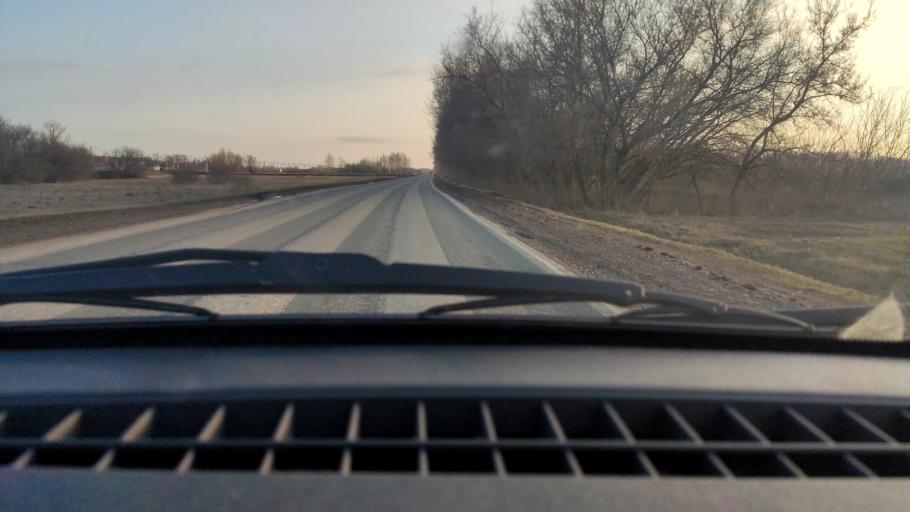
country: RU
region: Bashkortostan
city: Chishmy
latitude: 54.4543
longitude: 55.2507
